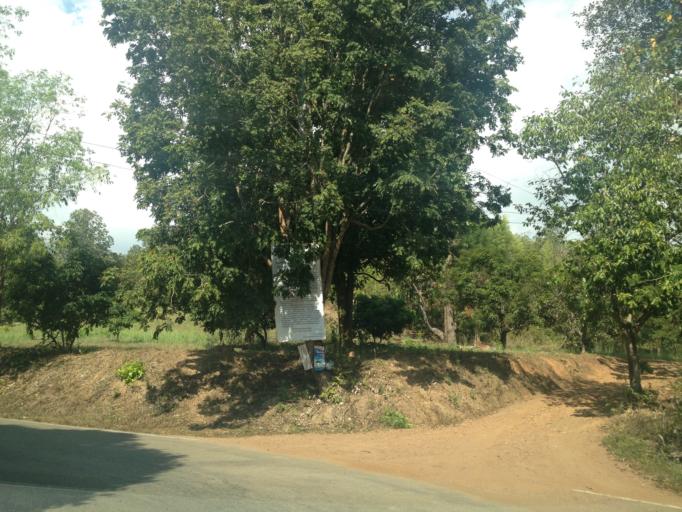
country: TH
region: Chiang Mai
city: Hang Dong
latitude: 18.7142
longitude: 98.8962
